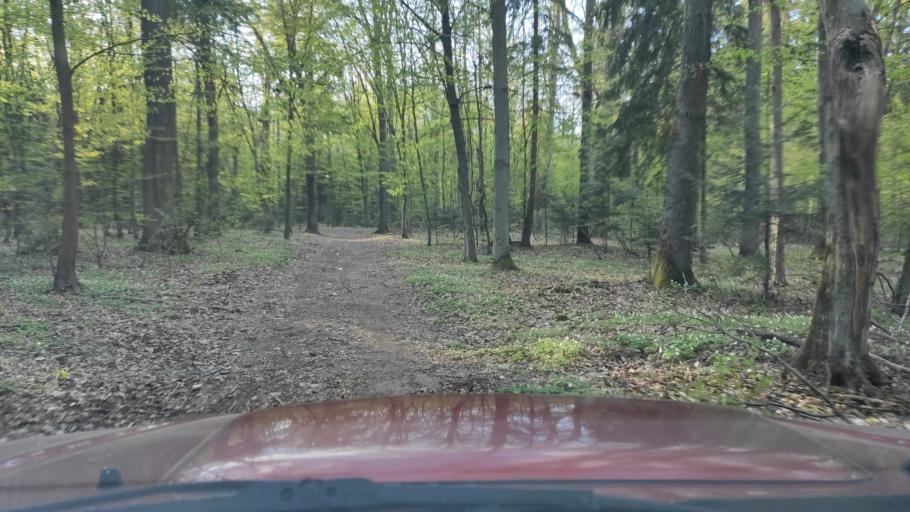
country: PL
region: Masovian Voivodeship
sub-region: Powiat radomski
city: Pionki
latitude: 51.4739
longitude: 21.4366
